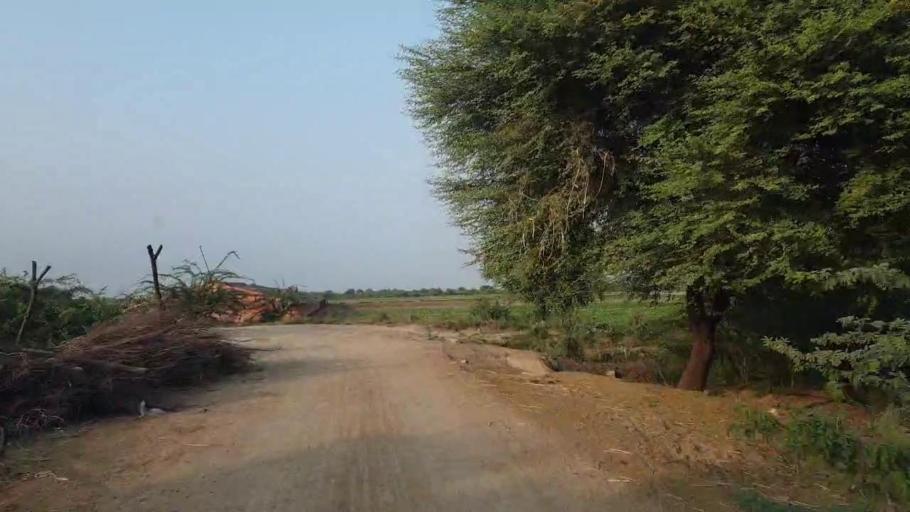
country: PK
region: Sindh
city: Rajo Khanani
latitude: 25.0348
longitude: 68.9763
